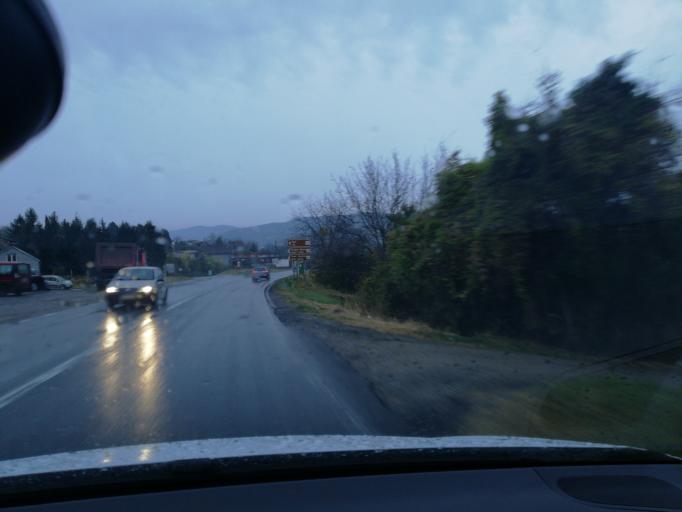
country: RS
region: Autonomna Pokrajina Vojvodina
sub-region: Juznobacki Okrug
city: Novi Sad
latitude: 45.2070
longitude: 19.8444
